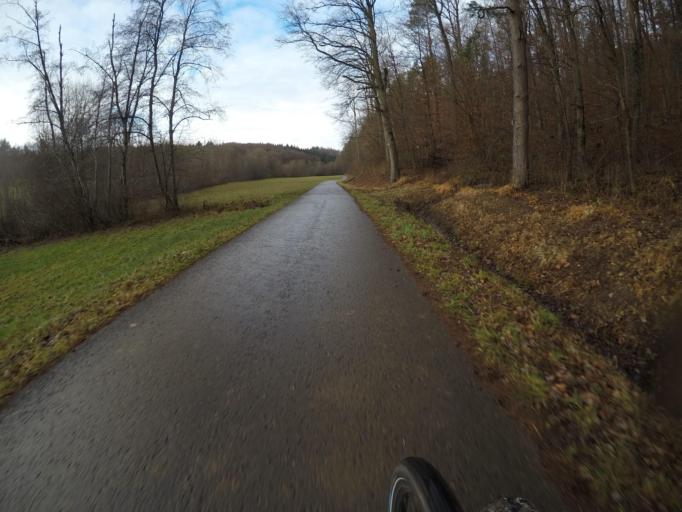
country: DE
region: Baden-Wuerttemberg
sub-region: Regierungsbezirk Stuttgart
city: Owen
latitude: 48.5853
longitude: 9.4275
